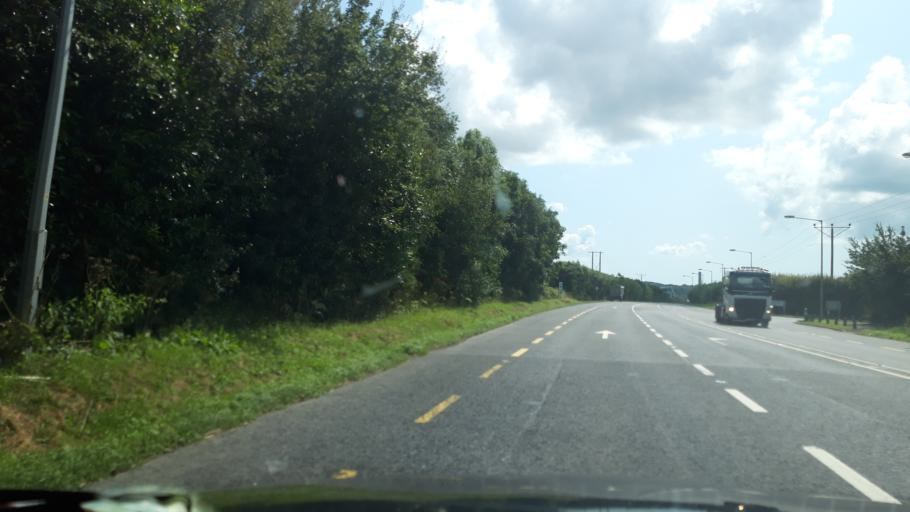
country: IE
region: Munster
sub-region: Waterford
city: Waterford
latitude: 52.2715
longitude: -7.0459
